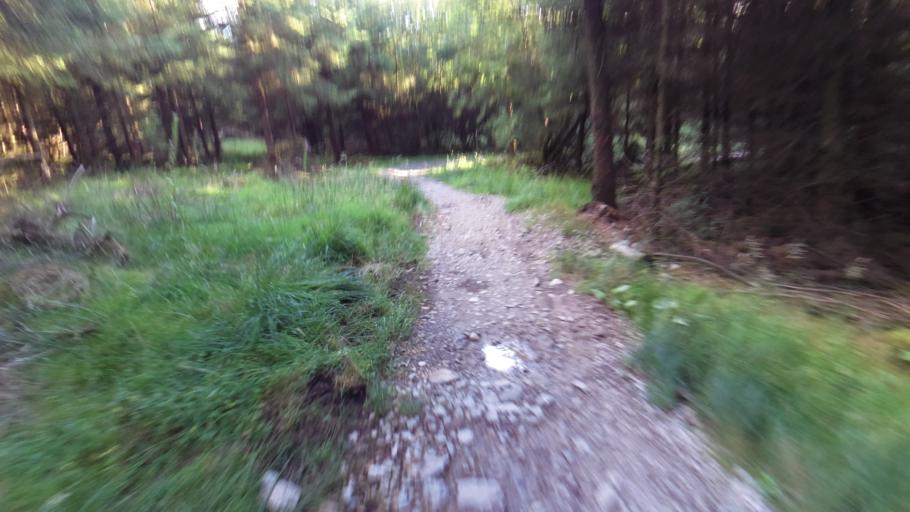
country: GB
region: England
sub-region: Lancashire
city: Clitheroe
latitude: 53.9963
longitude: -2.3949
